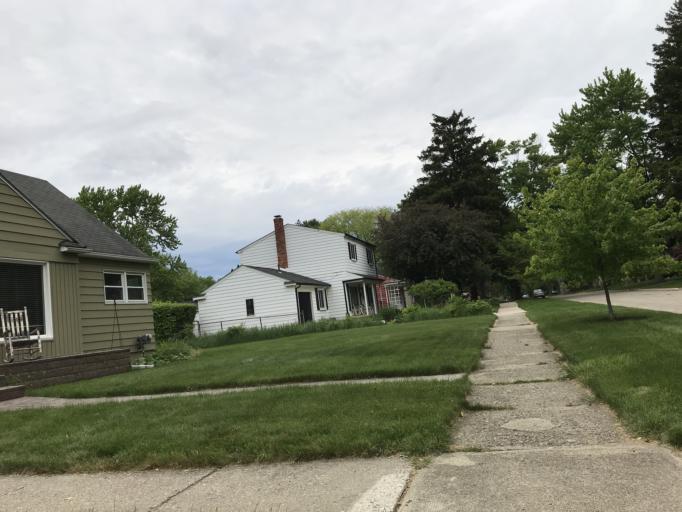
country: US
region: Michigan
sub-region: Oakland County
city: Farmington
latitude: 42.4580
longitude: -83.3541
